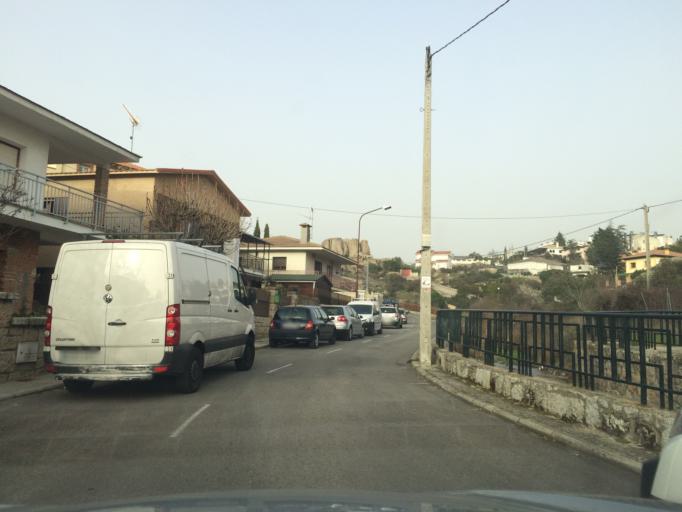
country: ES
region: Madrid
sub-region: Provincia de Madrid
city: Manzanares el Real
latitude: 40.7307
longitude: -3.8636
